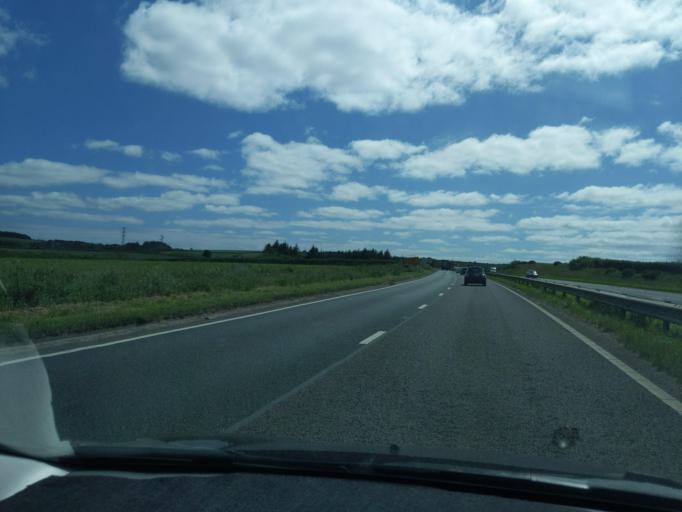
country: GB
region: England
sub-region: Cornwall
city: Probus
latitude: 50.3587
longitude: -4.9891
